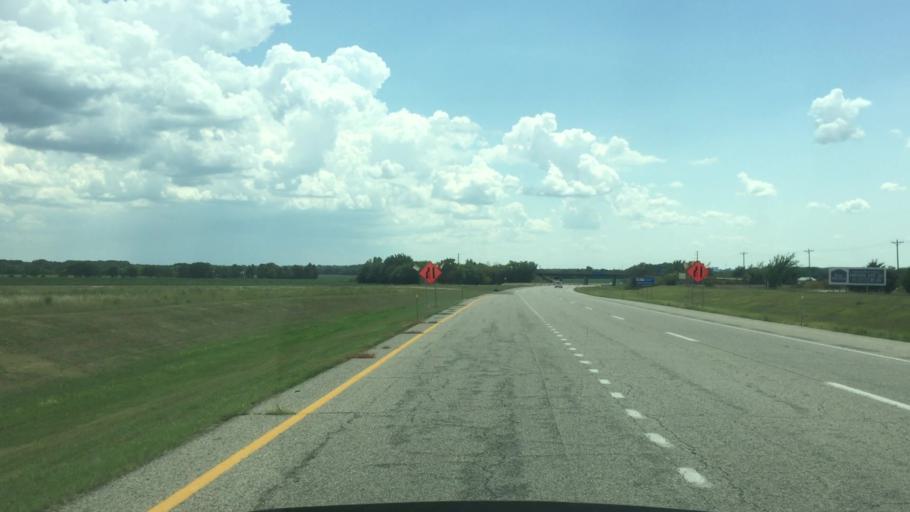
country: US
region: Kansas
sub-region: Lyon County
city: Emporia
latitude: 38.4680
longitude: -96.1881
